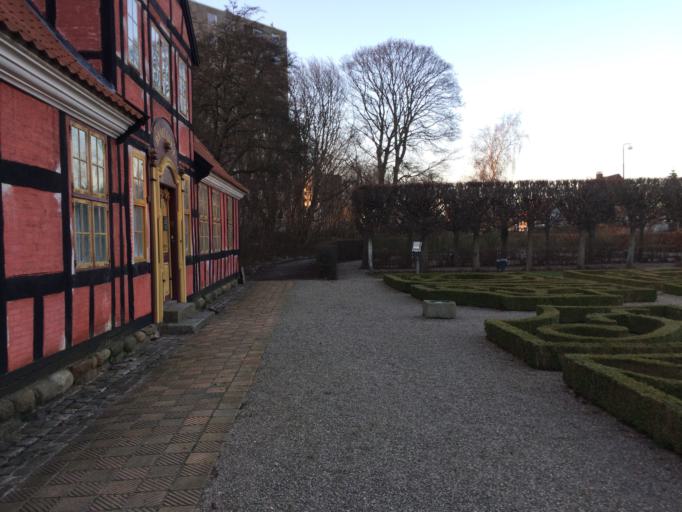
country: DK
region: South Denmark
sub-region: Fredericia Kommune
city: Fredericia
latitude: 55.5648
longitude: 9.7450
